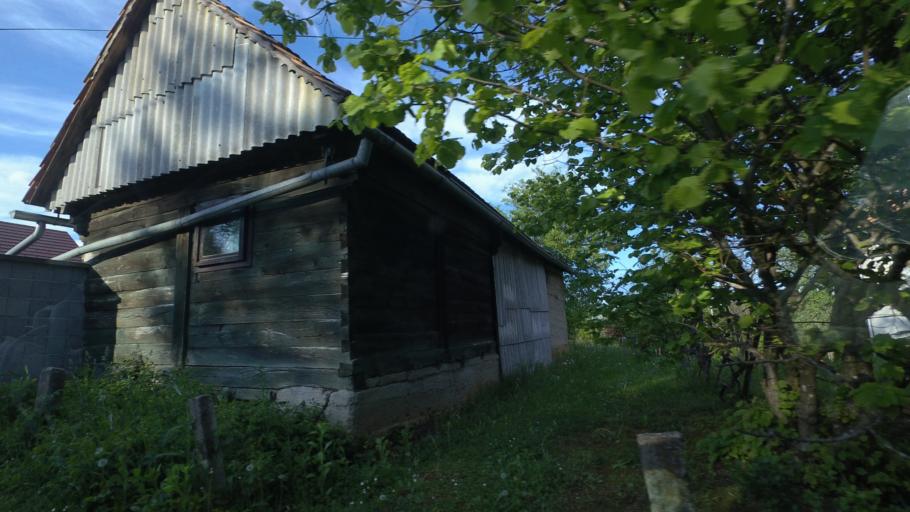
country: HR
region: Karlovacka
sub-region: Grad Karlovac
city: Karlovac
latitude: 45.3839
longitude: 15.5871
